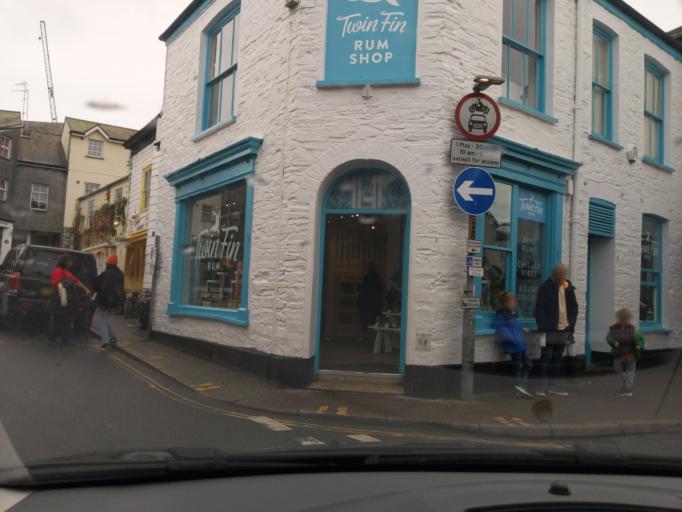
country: GB
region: England
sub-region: Cornwall
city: Padstow
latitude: 50.5408
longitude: -4.9384
